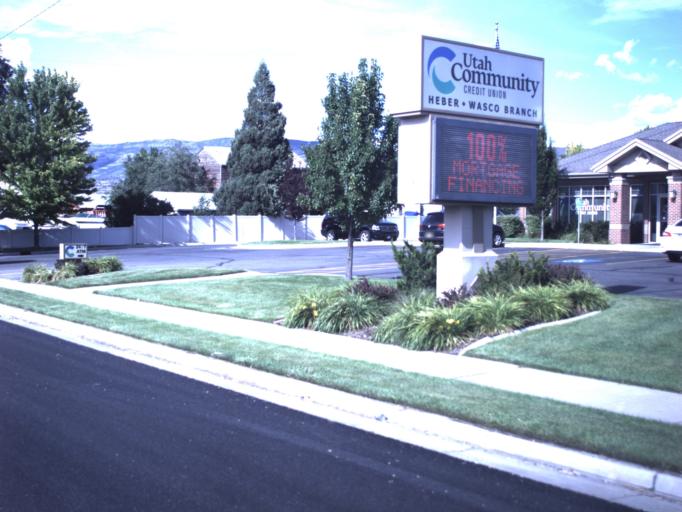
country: US
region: Utah
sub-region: Wasatch County
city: Heber
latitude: 40.4957
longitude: -111.4135
